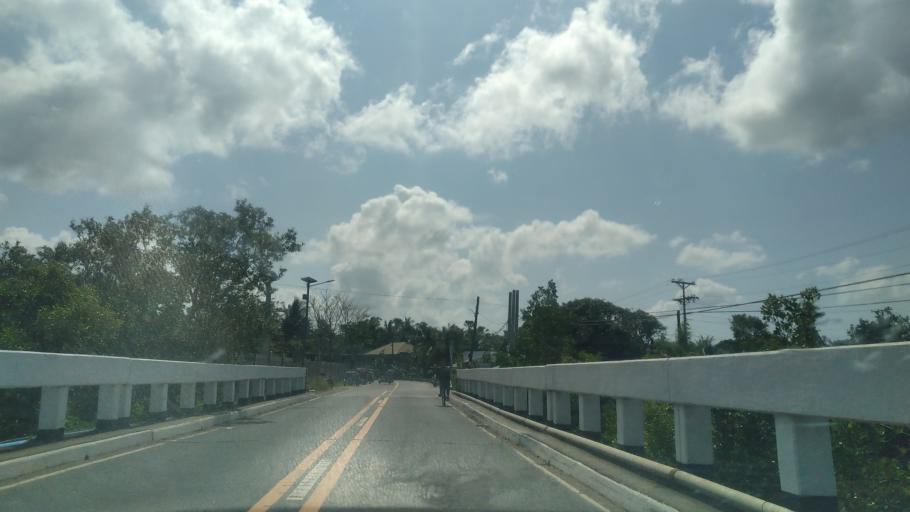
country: PH
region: Calabarzon
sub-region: Province of Quezon
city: Unisan
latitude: 13.8342
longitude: 121.9798
